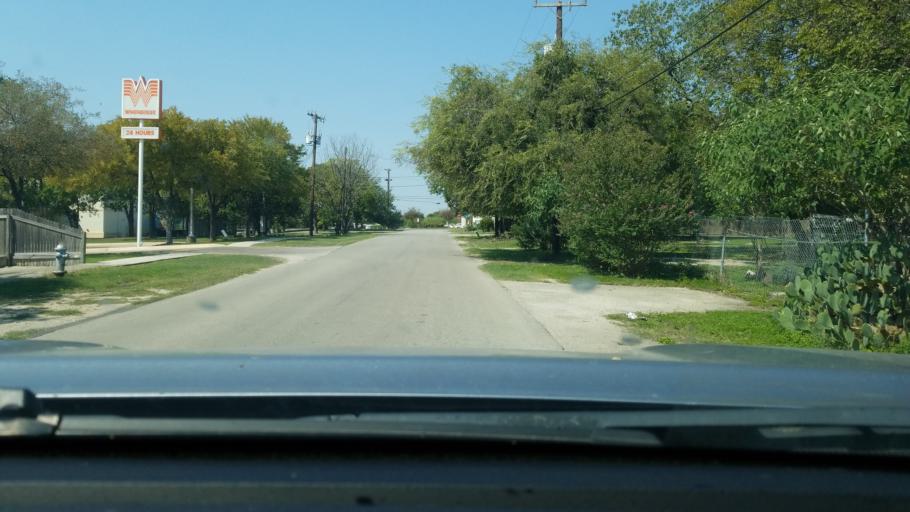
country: US
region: Texas
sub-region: Bexar County
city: Leon Valley
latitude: 29.5434
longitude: -98.6132
